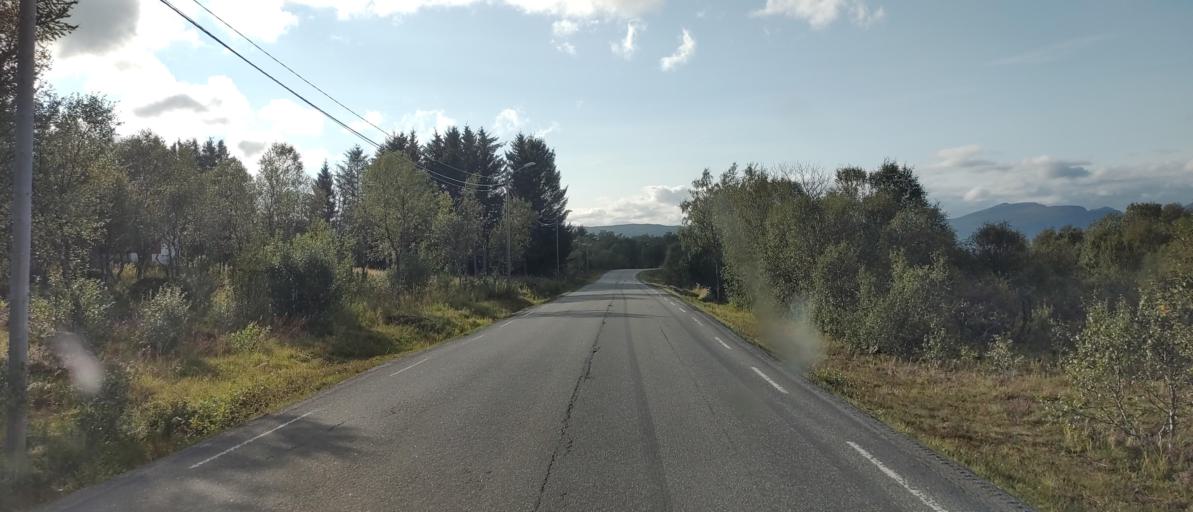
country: NO
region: Nordland
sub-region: Sortland
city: Sortland
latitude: 68.7210
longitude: 15.5053
